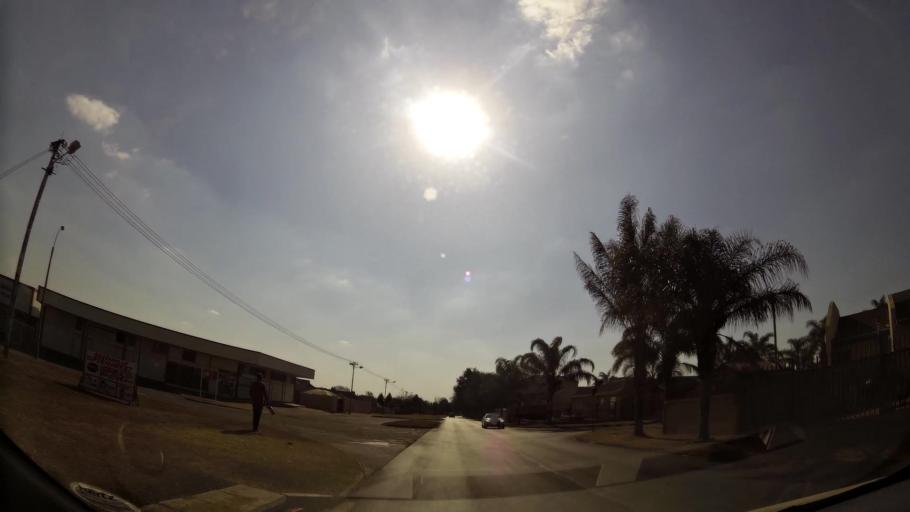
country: ZA
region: Gauteng
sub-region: West Rand District Municipality
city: Randfontein
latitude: -26.1594
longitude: 27.6931
